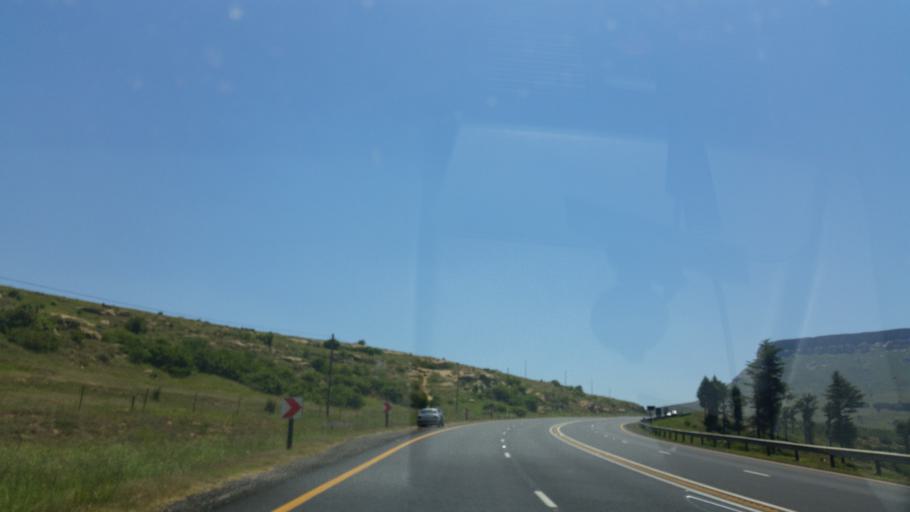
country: ZA
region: Orange Free State
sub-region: Thabo Mofutsanyana District Municipality
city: Harrismith
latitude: -28.2492
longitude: 29.1159
